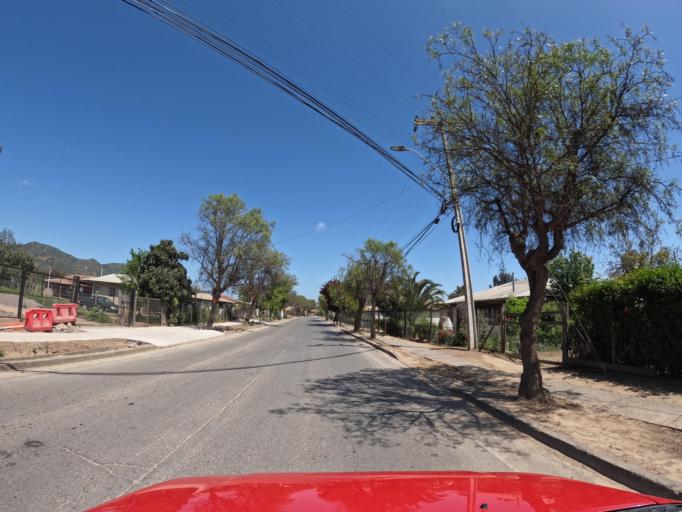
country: CL
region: O'Higgins
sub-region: Provincia de Colchagua
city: Santa Cruz
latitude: -34.7275
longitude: -71.6616
